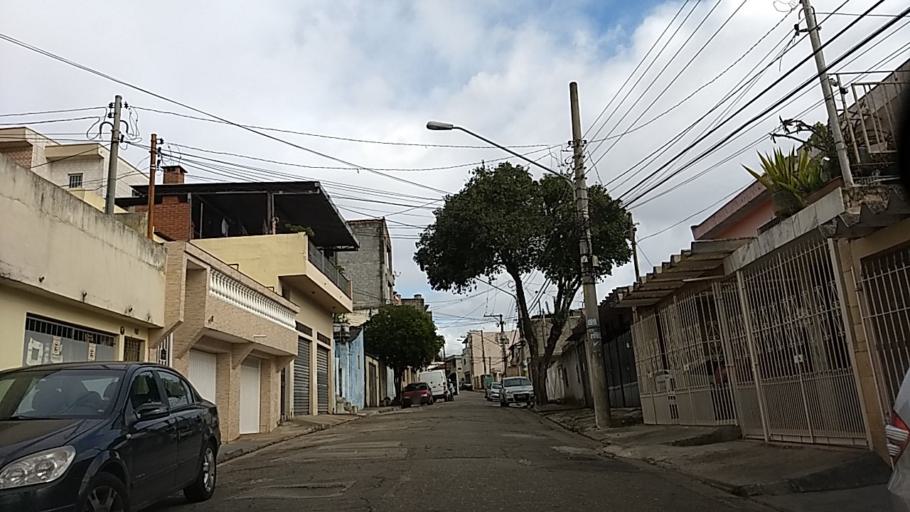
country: BR
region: Sao Paulo
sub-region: Guarulhos
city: Guarulhos
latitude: -23.4950
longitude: -46.5885
